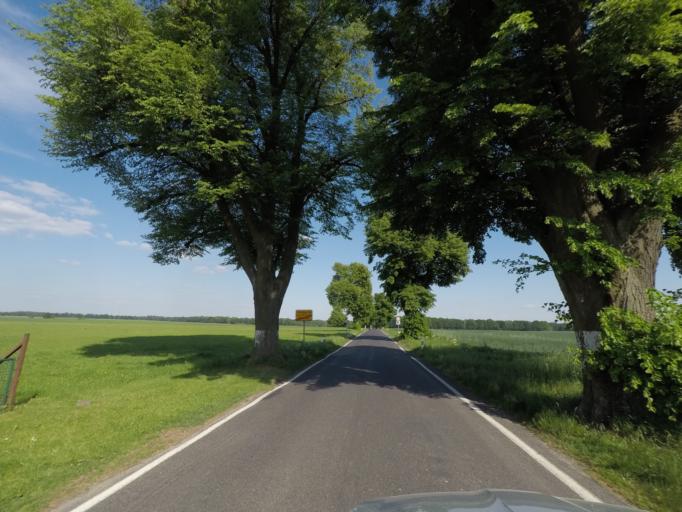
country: DE
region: Brandenburg
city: Hohenfinow
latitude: 52.7264
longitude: 13.8759
